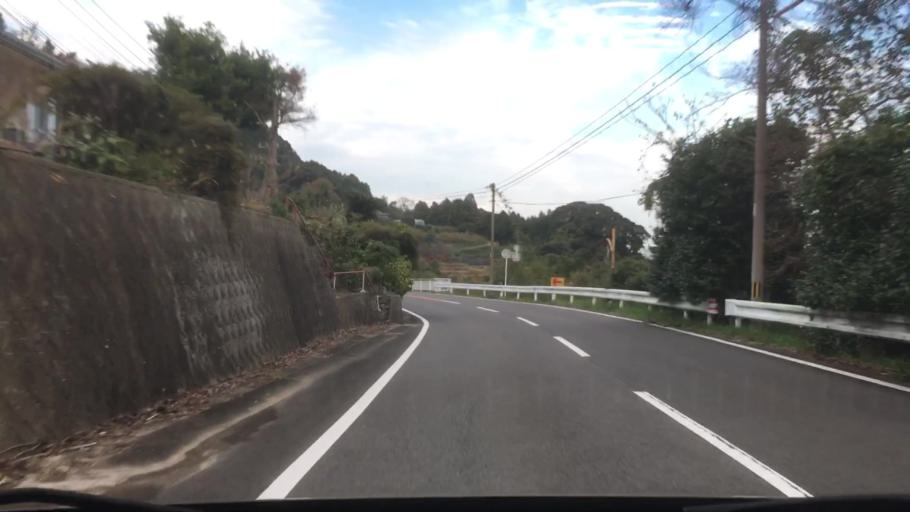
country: JP
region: Nagasaki
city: Sasebo
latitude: 32.9862
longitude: 129.7194
